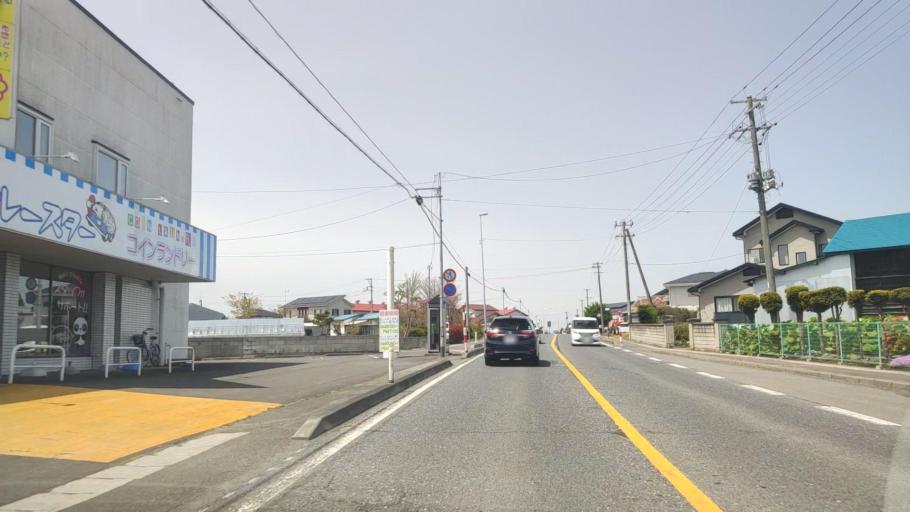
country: JP
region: Aomori
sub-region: Misawa Shi
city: Inuotose
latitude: 40.6077
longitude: 141.2866
